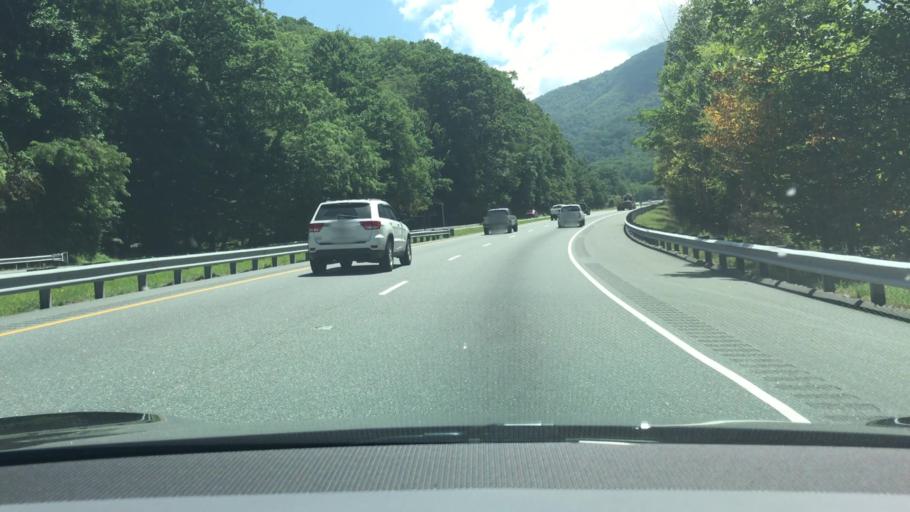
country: US
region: North Carolina
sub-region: Haywood County
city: Maggie Valley
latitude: 35.4330
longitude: -83.0929
